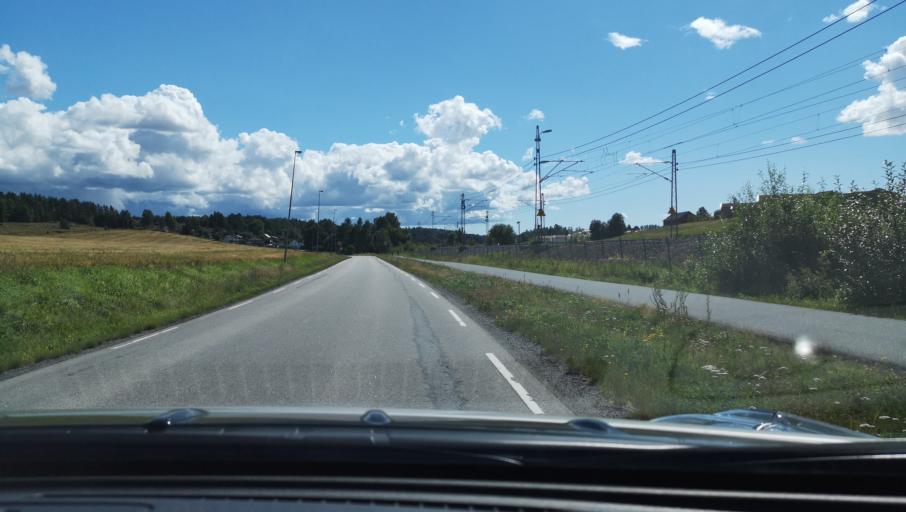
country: NO
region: Akershus
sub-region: As
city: As
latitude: 59.6604
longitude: 10.7965
